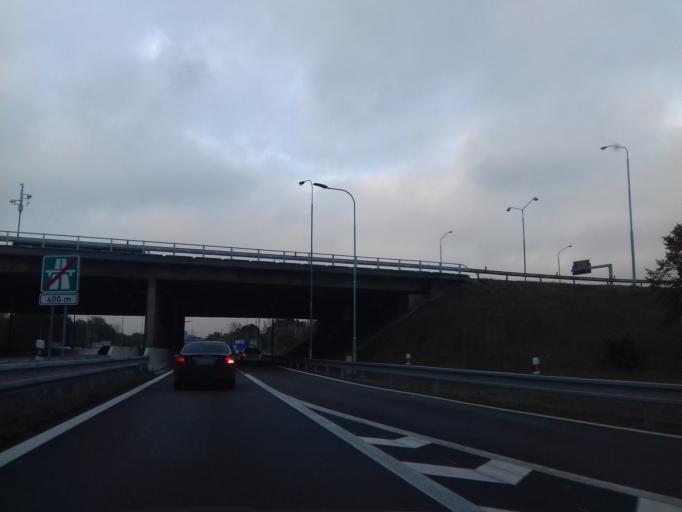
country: CZ
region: South Moravian
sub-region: Mesto Brno
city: Brno
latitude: 49.1589
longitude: 16.6312
